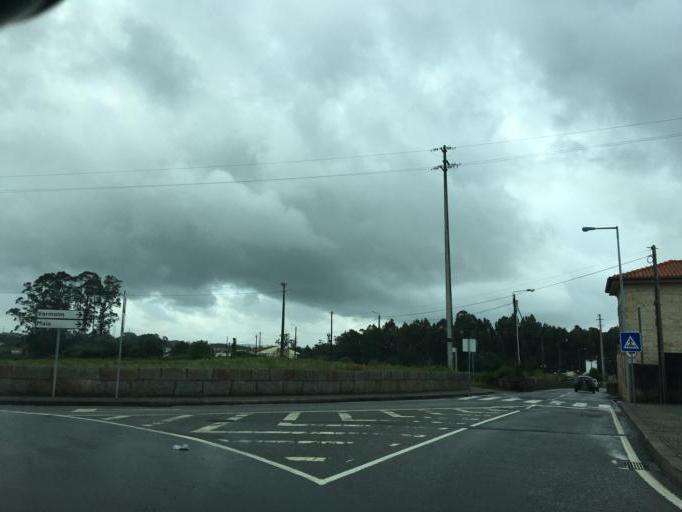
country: PT
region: Porto
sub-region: Maia
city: Nogueira
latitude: 41.2530
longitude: -8.5923
